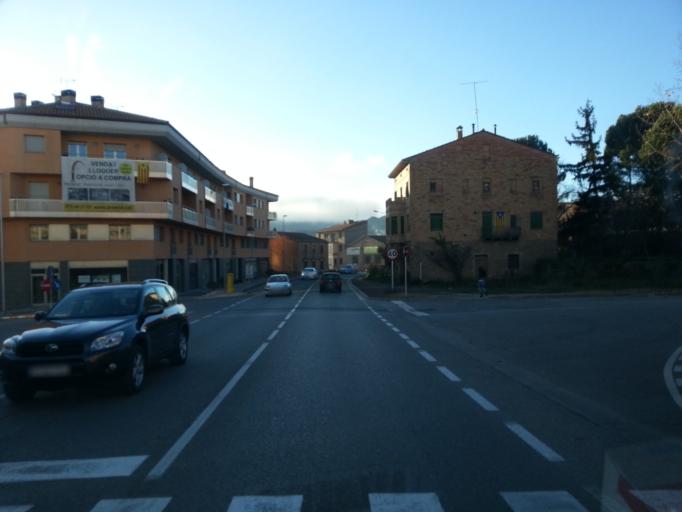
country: ES
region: Catalonia
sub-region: Provincia de Lleida
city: Solsona
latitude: 41.9939
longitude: 1.5245
